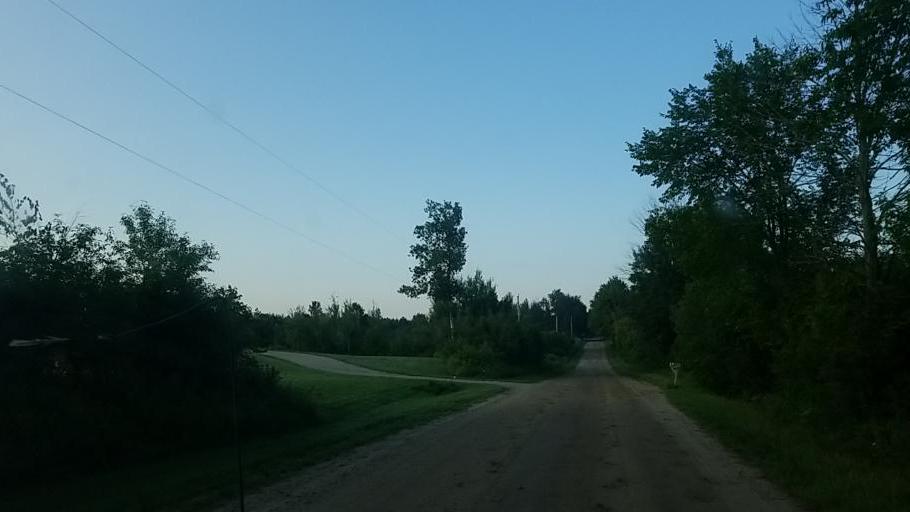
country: US
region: Michigan
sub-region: Osceola County
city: Evart
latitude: 43.9041
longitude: -85.1677
